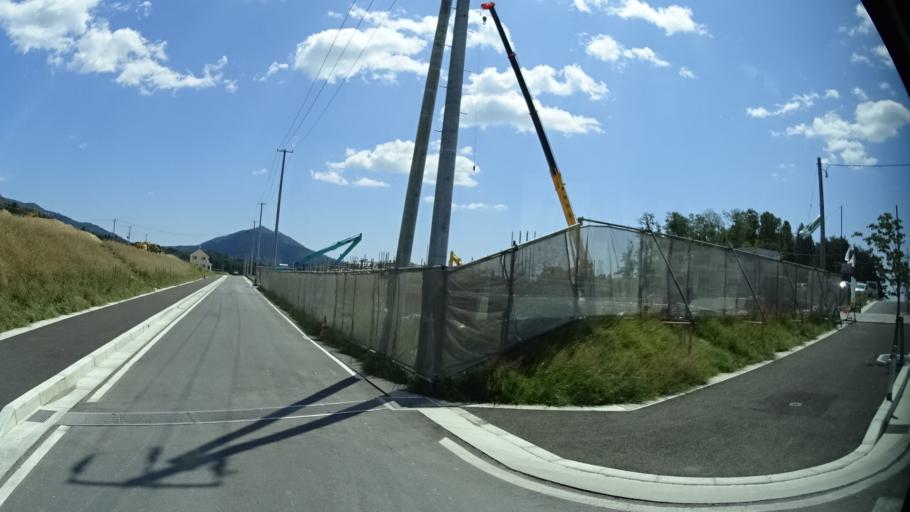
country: JP
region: Iwate
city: Ofunato
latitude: 39.0238
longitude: 141.6399
